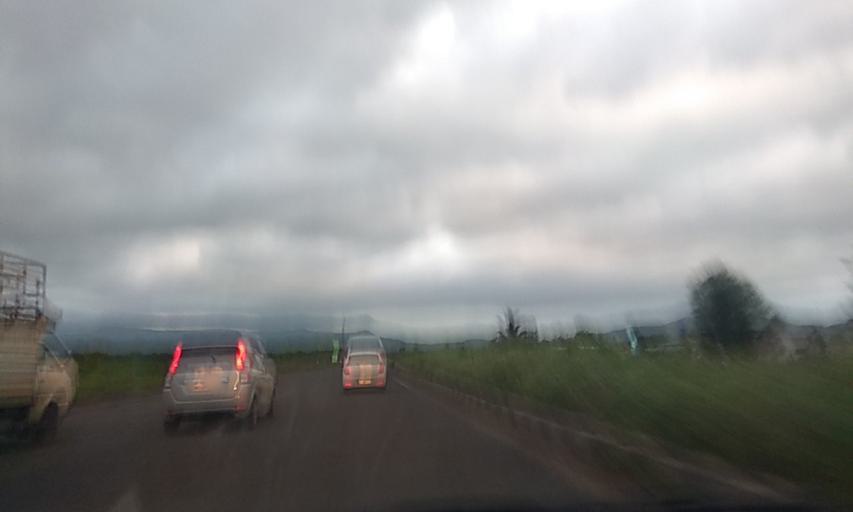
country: IN
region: Maharashtra
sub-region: Satara Division
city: Wai
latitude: 17.9379
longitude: 73.9770
